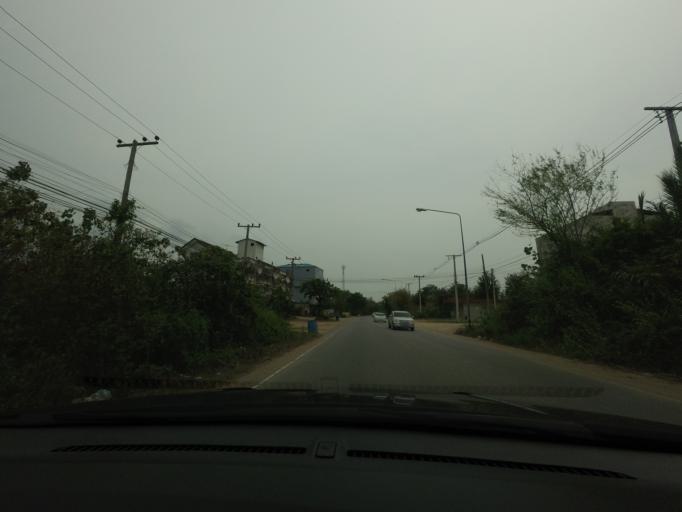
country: TH
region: Phetchaburi
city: Ban Laem
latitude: 13.2026
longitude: 99.9590
